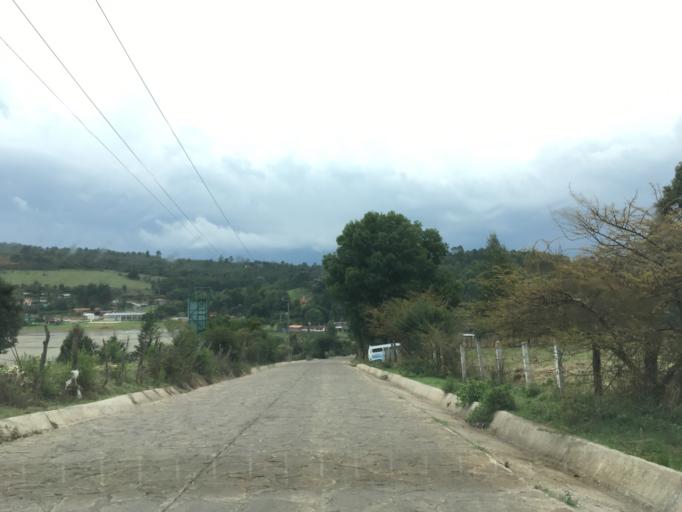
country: MX
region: Michoacan
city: Acuitzio del Canje
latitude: 19.5292
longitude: -101.2493
